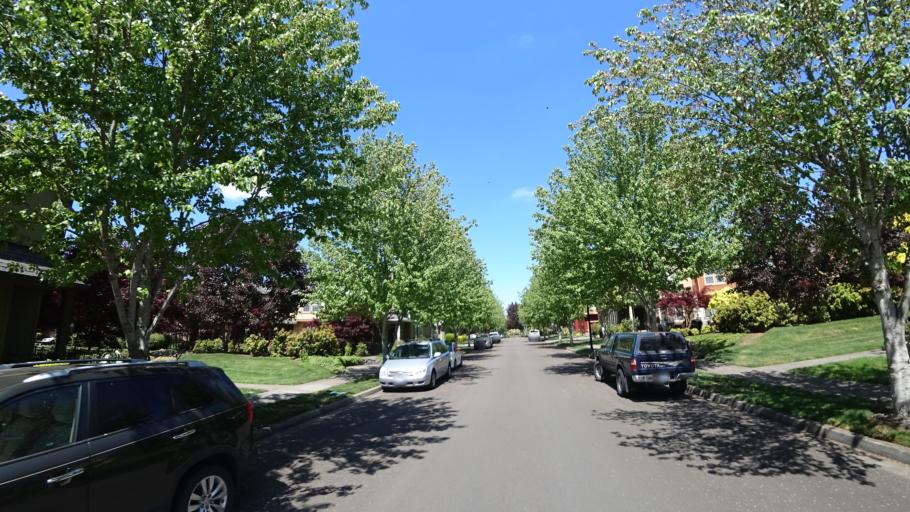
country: US
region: Oregon
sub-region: Washington County
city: Hillsboro
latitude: 45.5077
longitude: -122.9717
